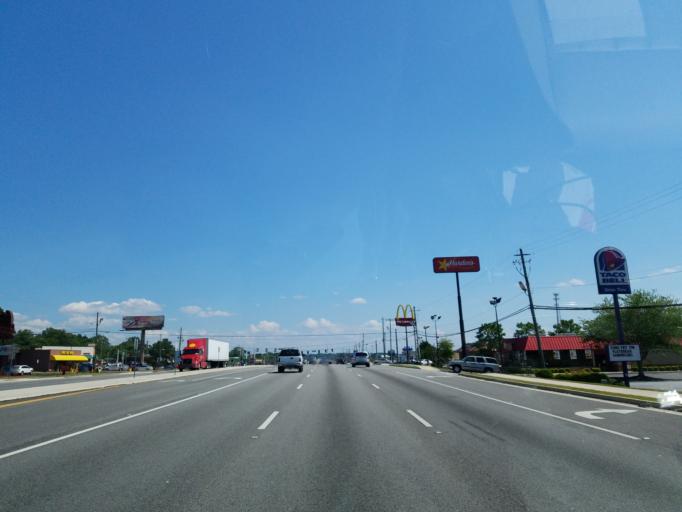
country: US
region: Georgia
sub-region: Spalding County
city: Experiment
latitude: 33.2765
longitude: -84.2915
